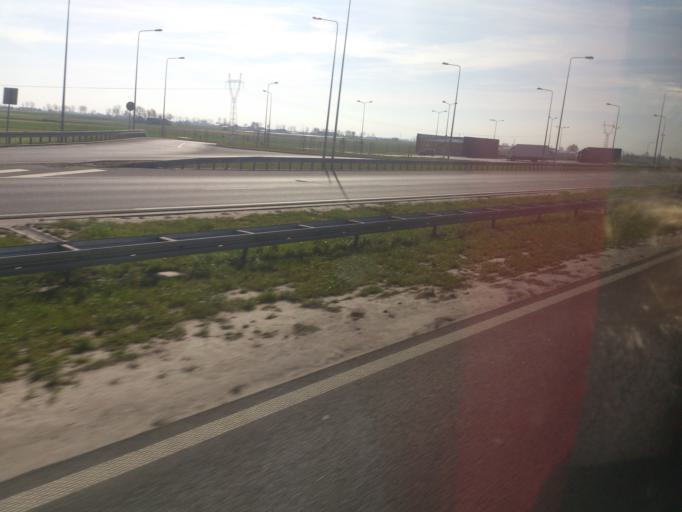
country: PL
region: Kujawsko-Pomorskie
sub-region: Powiat aleksandrowski
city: Waganiec
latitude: 52.7624
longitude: 18.8539
